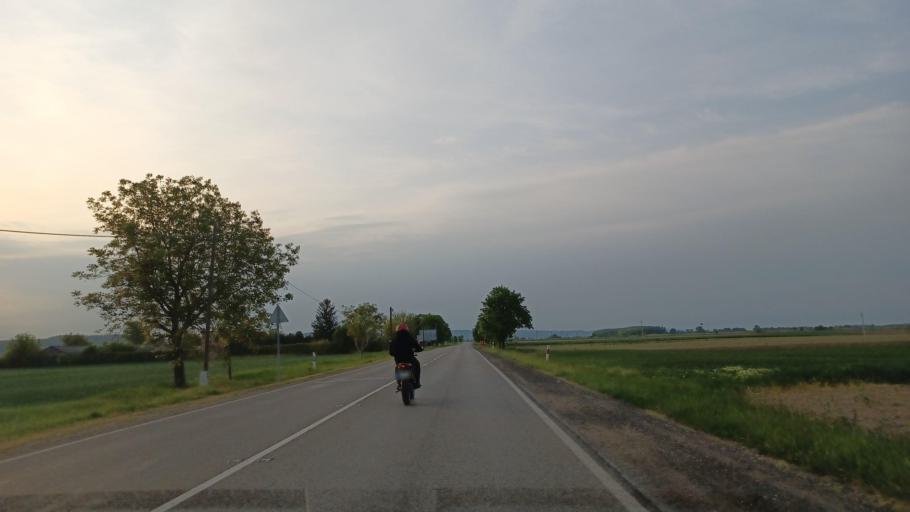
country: HU
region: Tolna
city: Bataszek
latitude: 46.2076
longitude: 18.7195
